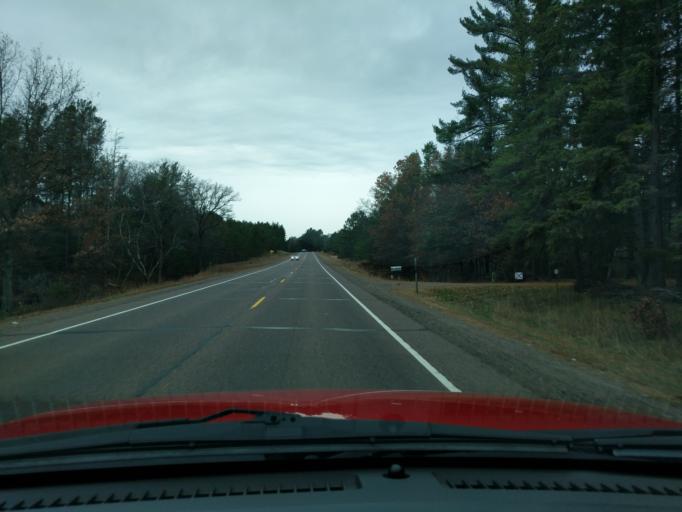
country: US
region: Wisconsin
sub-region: Washburn County
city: Spooner
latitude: 45.8232
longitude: -91.9336
